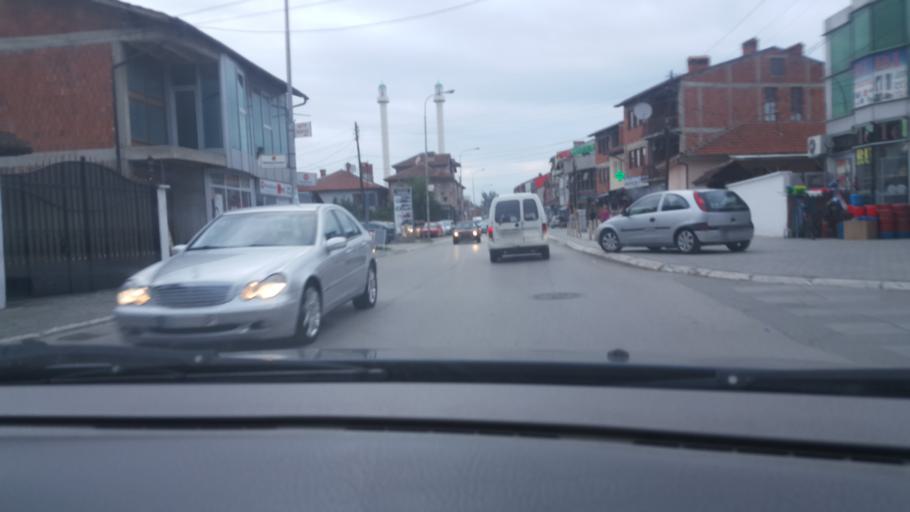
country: XK
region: Gjakova
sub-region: Komuna e Gjakoves
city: Gjakove
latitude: 42.3897
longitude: 20.4265
